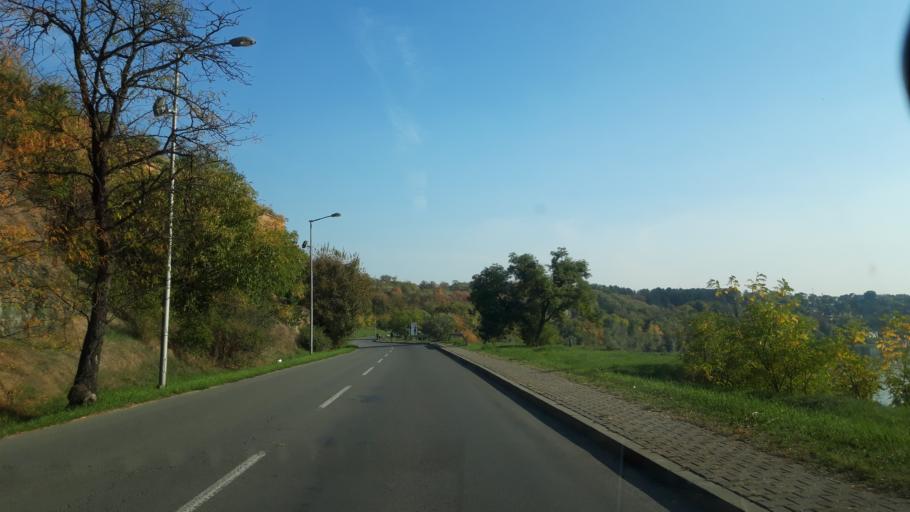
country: RS
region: Autonomna Pokrajina Vojvodina
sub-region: Juznobacki Okrug
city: Petrovaradin
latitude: 45.2501
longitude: 19.8626
